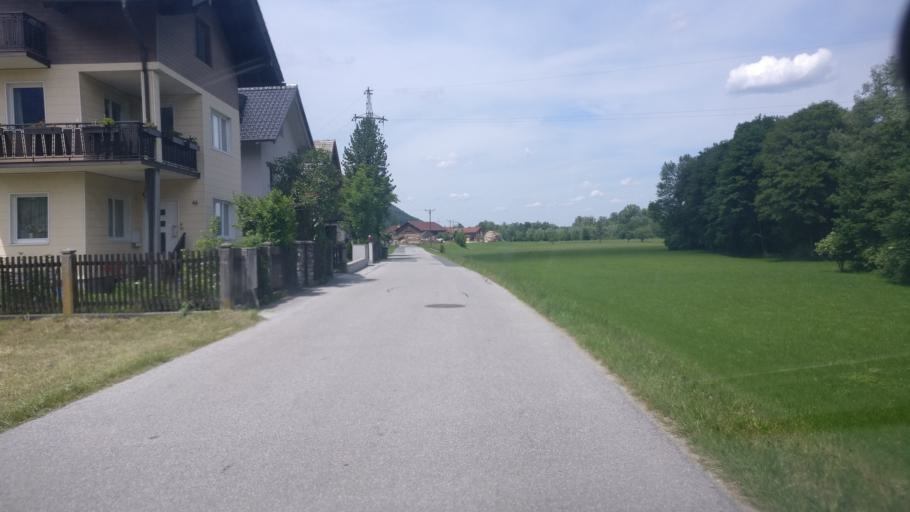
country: AT
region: Salzburg
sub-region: Politischer Bezirk Hallein
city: Kuchl
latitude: 47.6273
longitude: 13.1374
